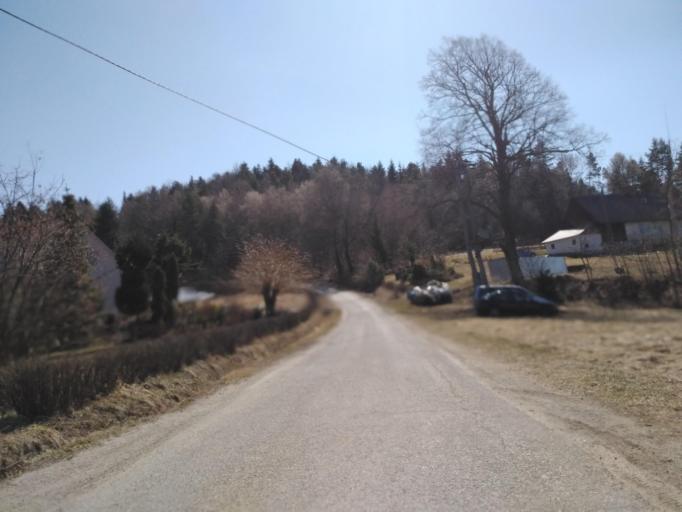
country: PL
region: Subcarpathian Voivodeship
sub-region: Powiat brzozowski
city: Jablonica Polska
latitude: 49.7344
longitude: 21.9004
